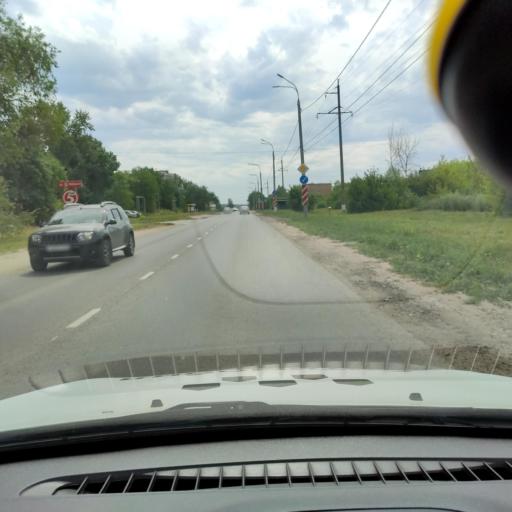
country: RU
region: Samara
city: Zhigulevsk
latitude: 53.4066
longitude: 49.5229
